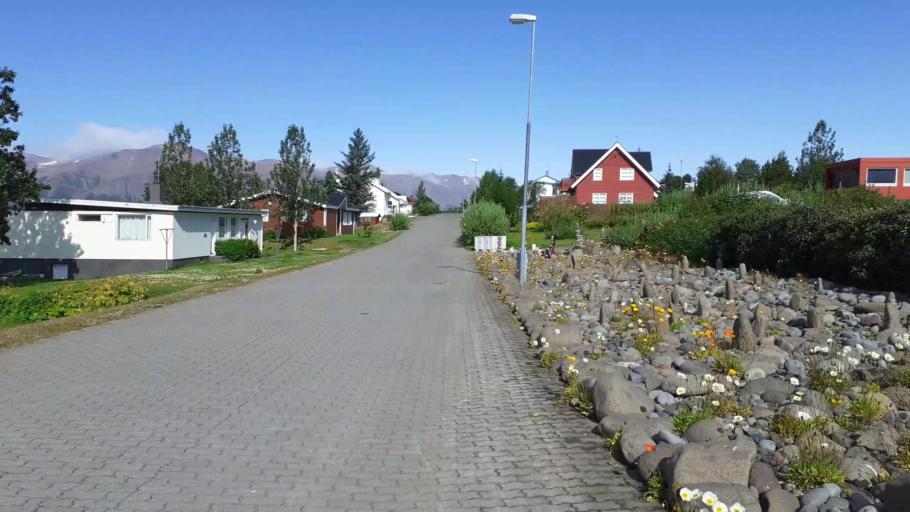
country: IS
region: Northeast
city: Dalvik
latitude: 65.9802
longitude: -18.3765
